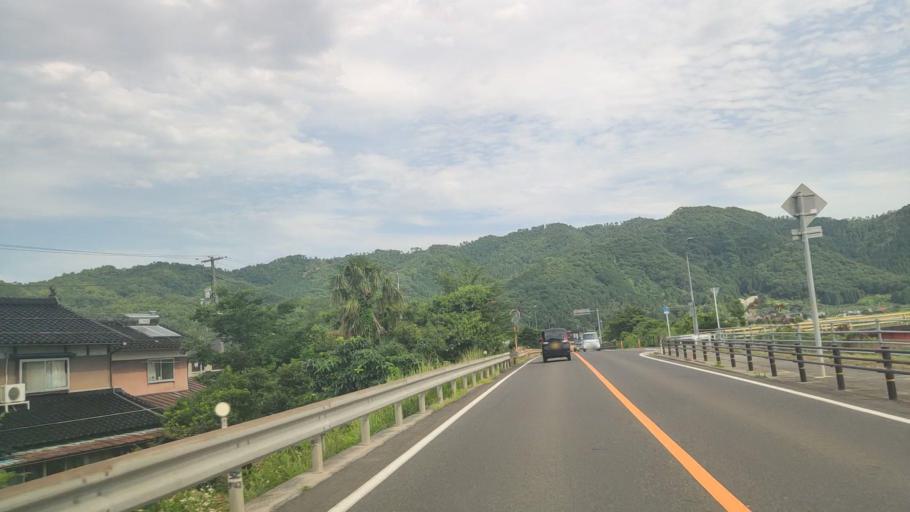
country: JP
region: Tottori
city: Tottori
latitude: 35.3769
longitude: 134.2124
